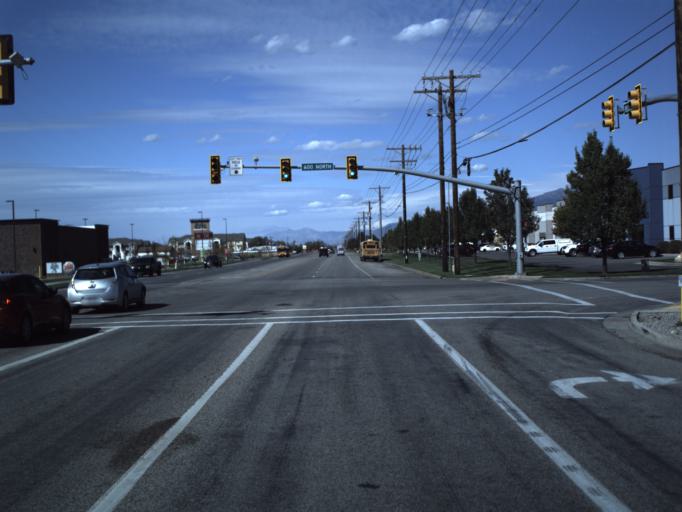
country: US
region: Utah
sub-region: Davis County
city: North Salt Lake
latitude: 40.8525
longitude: -111.9297
